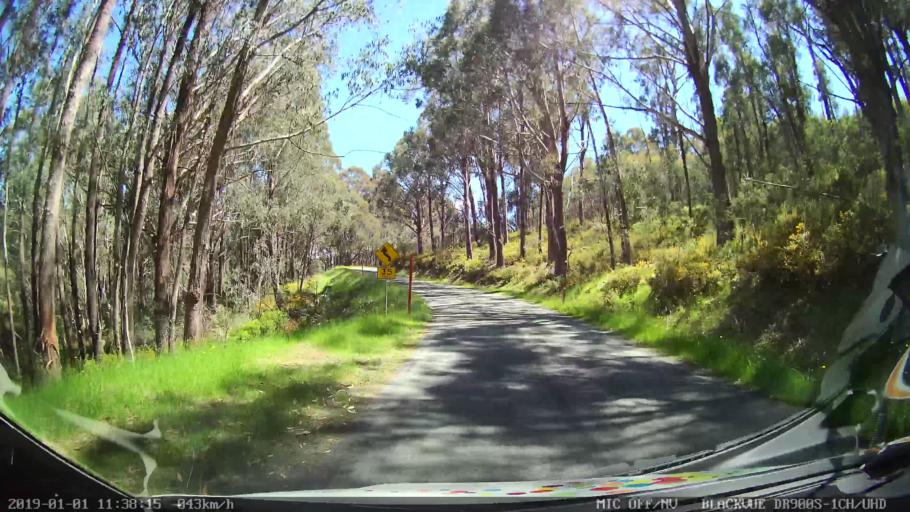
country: AU
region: New South Wales
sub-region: Snowy River
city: Jindabyne
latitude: -35.9354
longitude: 148.3871
